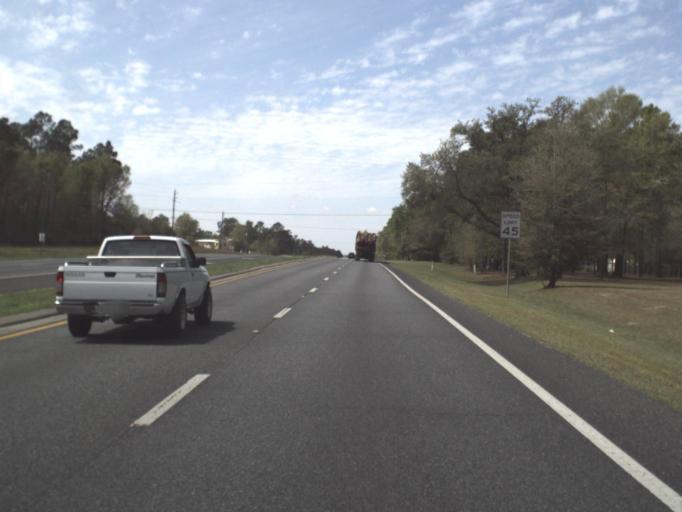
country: US
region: Florida
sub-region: Okaloosa County
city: Crestview
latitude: 30.7638
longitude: -86.6027
